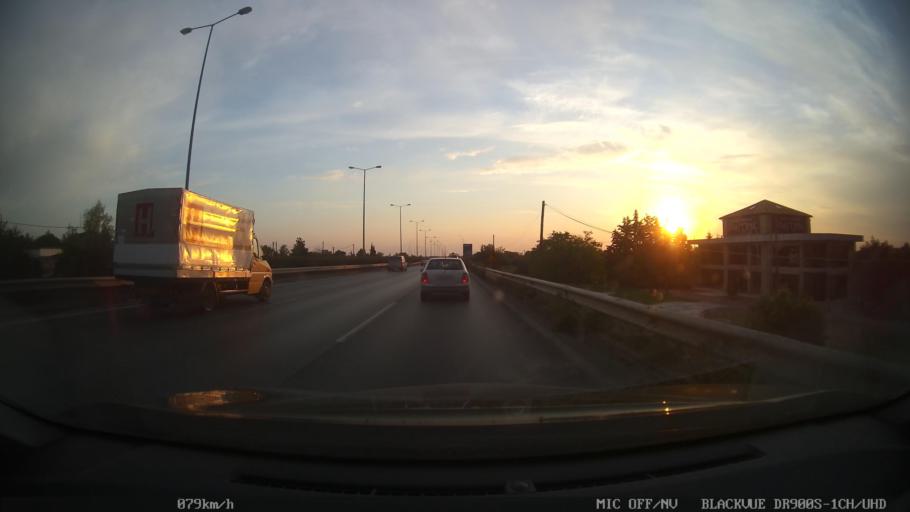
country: GR
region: Central Macedonia
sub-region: Nomos Thessalonikis
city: Pylaia
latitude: 40.5863
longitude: 22.9833
